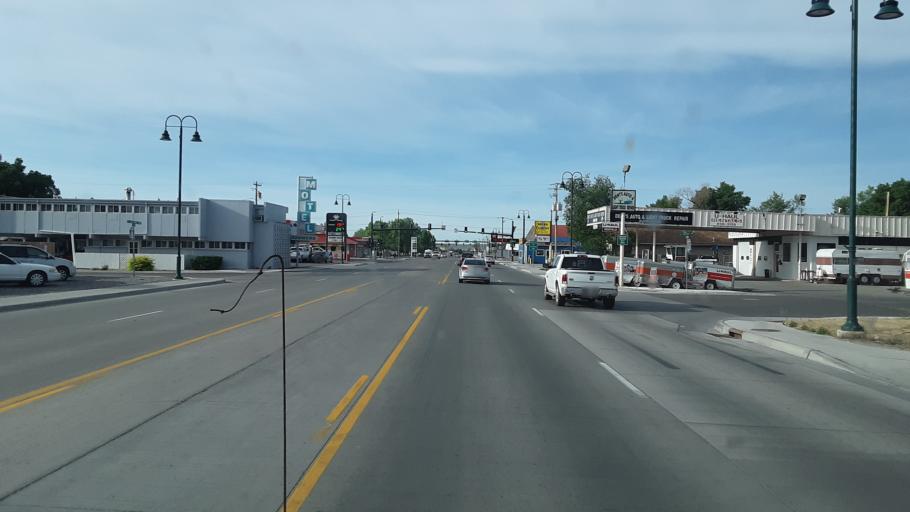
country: US
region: Wyoming
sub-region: Fremont County
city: Riverton
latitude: 43.0281
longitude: -108.3807
